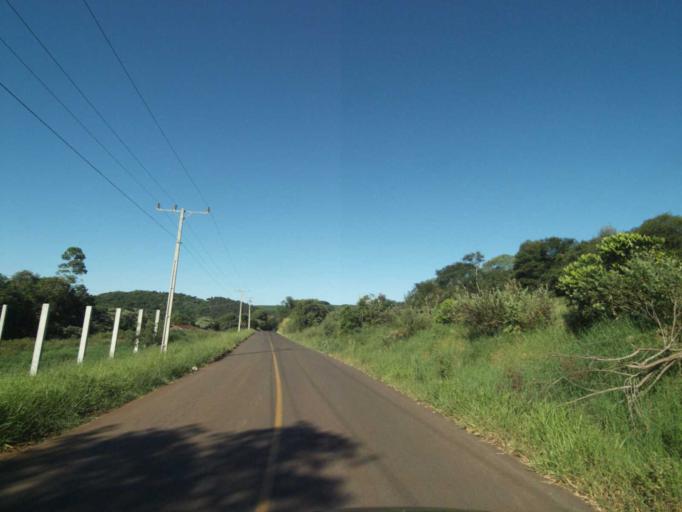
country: BR
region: Parana
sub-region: Coronel Vivida
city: Coronel Vivida
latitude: -25.9670
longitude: -52.8049
